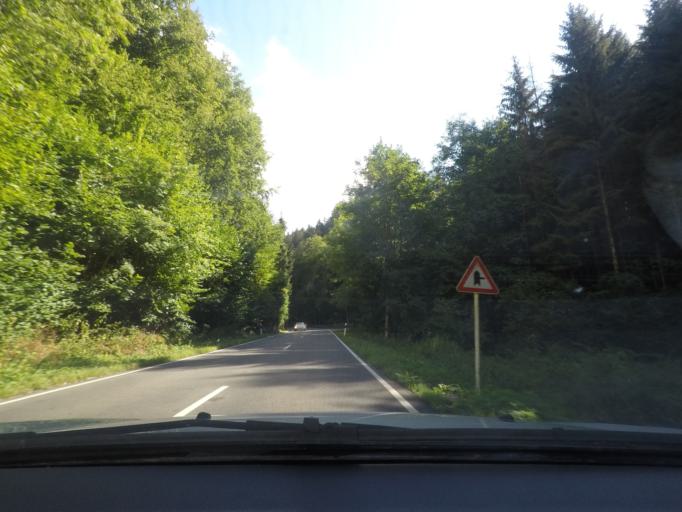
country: LU
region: Grevenmacher
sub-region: Canton d'Echternach
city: Waldbillig
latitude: 49.7661
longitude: 6.2823
